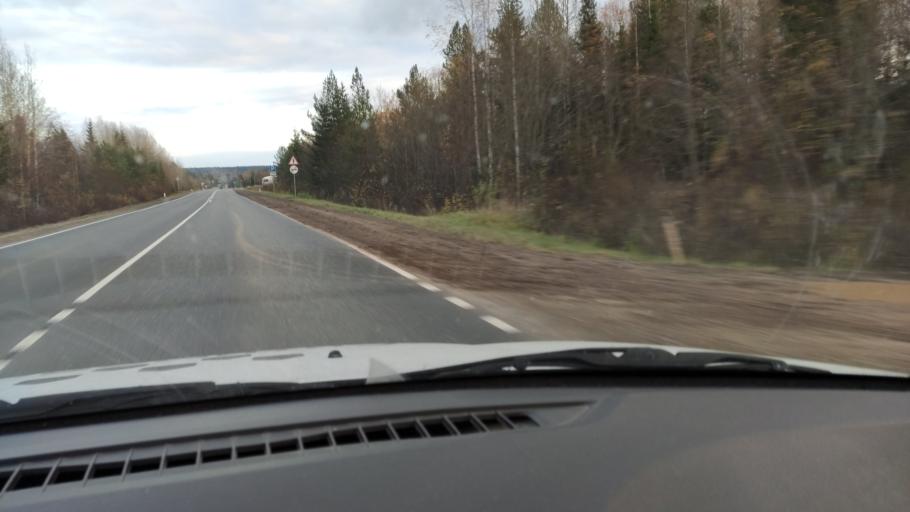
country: RU
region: Kirov
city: Omutninsk
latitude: 58.7012
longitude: 52.1132
